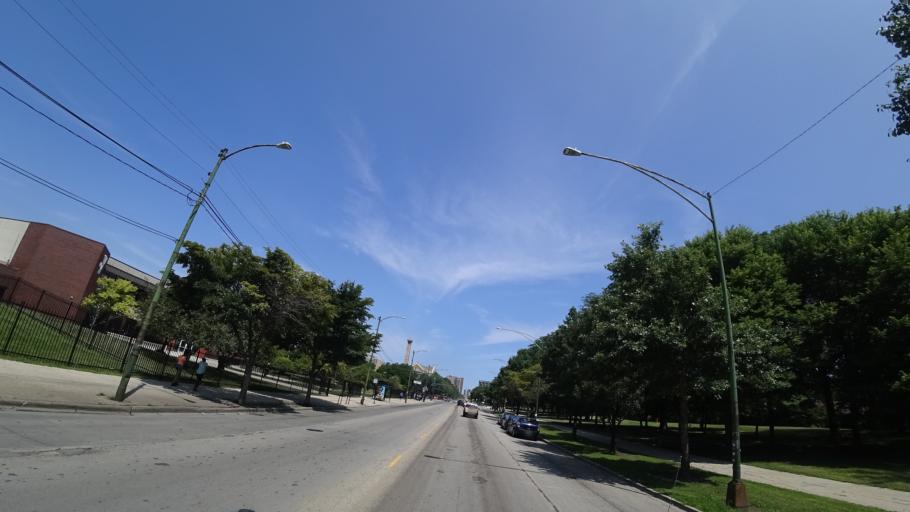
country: US
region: Illinois
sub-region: Cook County
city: Chicago
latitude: 41.7793
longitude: -87.5864
